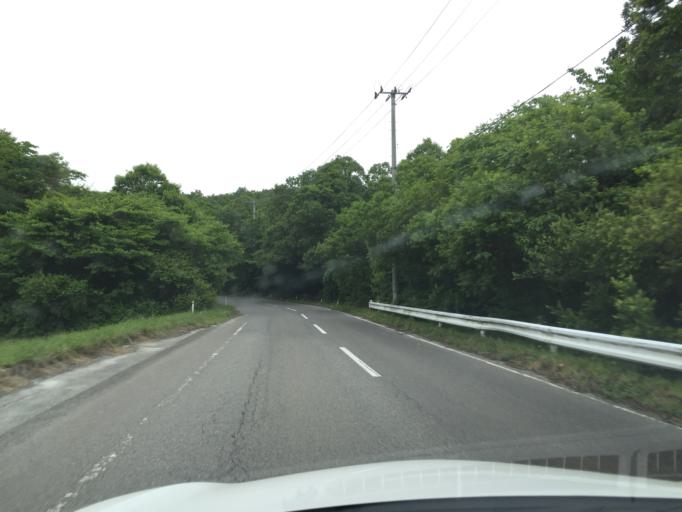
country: JP
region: Fukushima
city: Funehikimachi-funehiki
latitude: 37.3138
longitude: 140.7080
